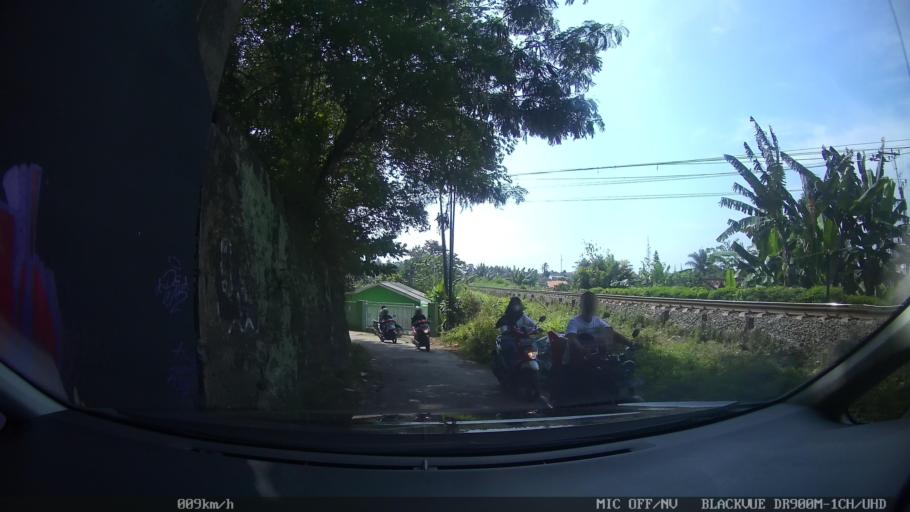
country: ID
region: Lampung
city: Kedaton
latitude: -5.3598
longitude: 105.2424
